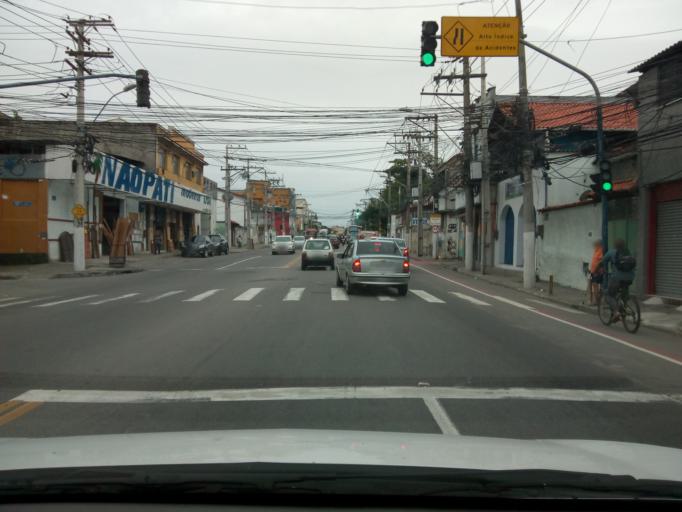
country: BR
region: Rio de Janeiro
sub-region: Niteroi
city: Niteroi
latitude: -22.8771
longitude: -43.1084
